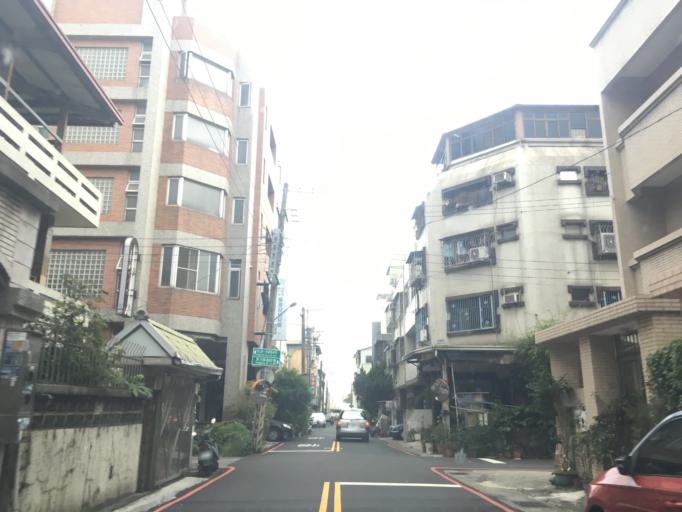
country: TW
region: Taiwan
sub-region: Taichung City
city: Taichung
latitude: 24.1679
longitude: 120.7019
